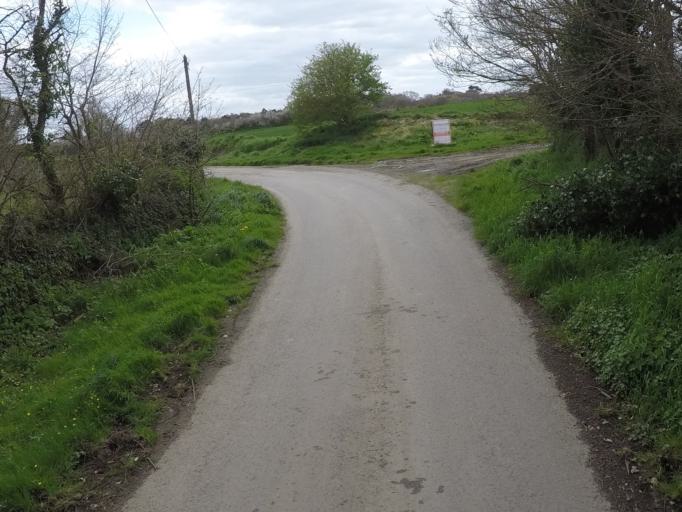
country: FR
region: Brittany
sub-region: Departement des Cotes-d'Armor
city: Plouezec
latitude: 48.7177
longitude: -2.9595
